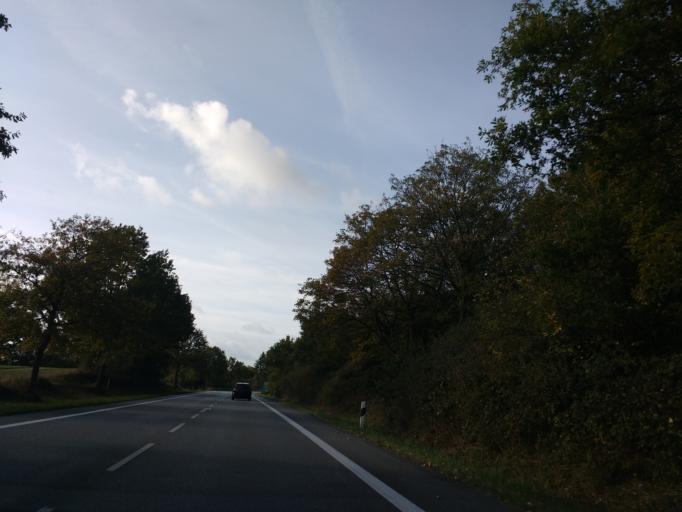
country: DE
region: Schleswig-Holstein
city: Schashagen
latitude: 54.1240
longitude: 10.8781
